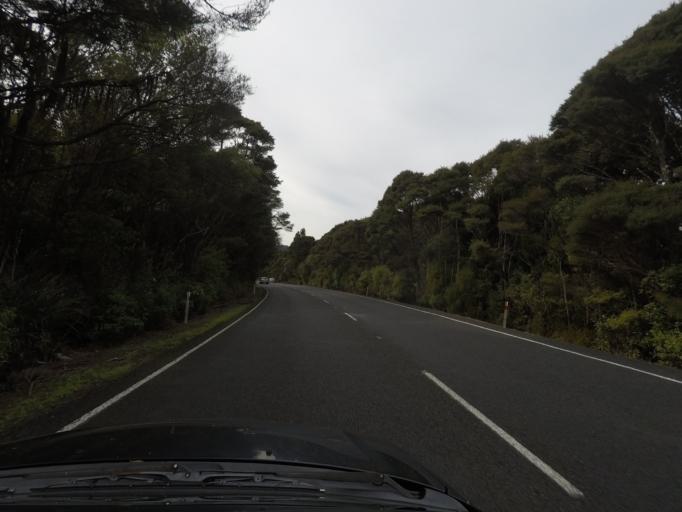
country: NZ
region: Auckland
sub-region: Auckland
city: Titirangi
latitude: -36.9420
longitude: 174.5522
